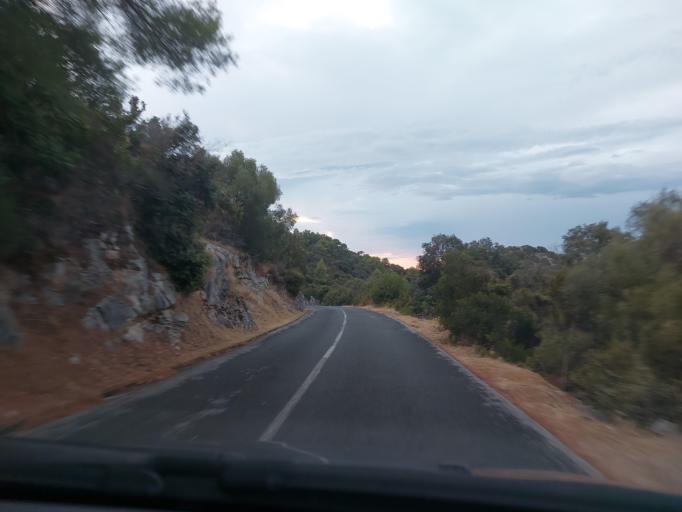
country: HR
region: Dubrovacko-Neretvanska
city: Smokvica
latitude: 42.7693
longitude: 16.8810
